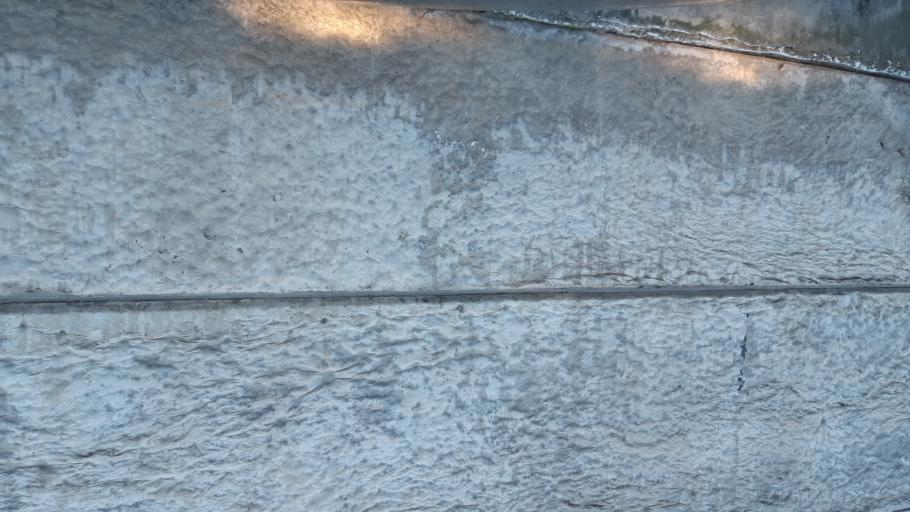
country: LT
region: Kauno apskritis
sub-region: Kaunas
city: Kaunas
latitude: 54.9144
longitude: 23.9025
